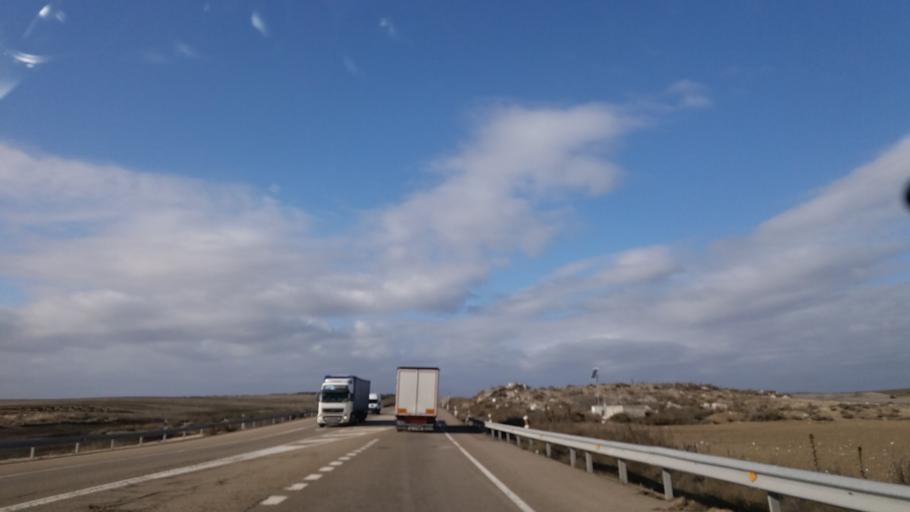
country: ES
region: Aragon
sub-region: Provincia de Zaragoza
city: Gelsa
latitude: 41.4954
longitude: -0.3536
